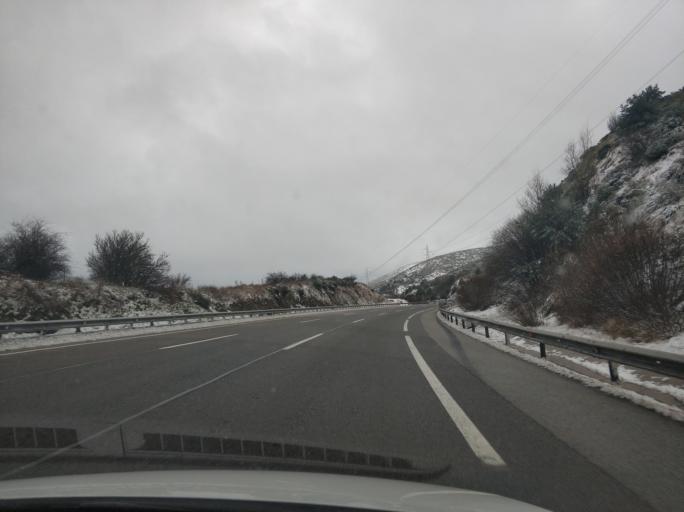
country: ES
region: Madrid
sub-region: Provincia de Madrid
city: Somosierra
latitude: 41.1594
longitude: -3.5849
